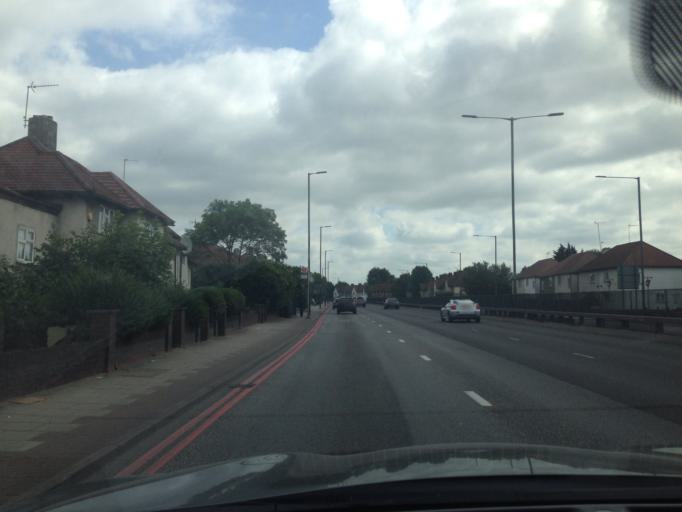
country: GB
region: England
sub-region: Greater London
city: Wembley
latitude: 51.5470
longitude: -0.2671
